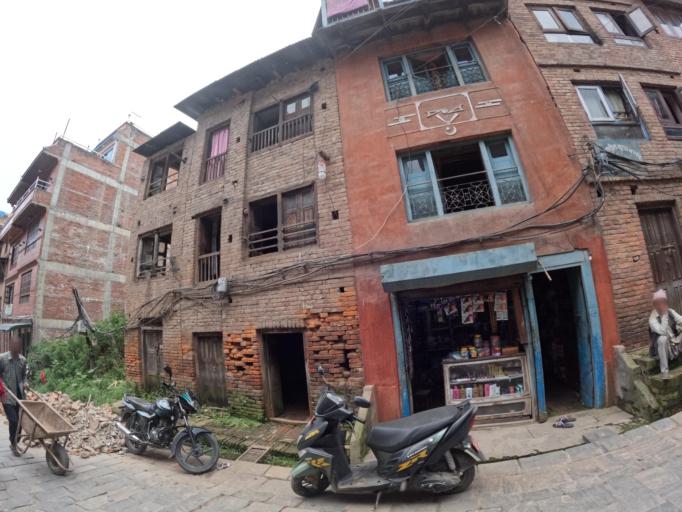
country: NP
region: Central Region
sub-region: Bagmati Zone
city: Bhaktapur
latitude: 27.6715
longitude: 85.4239
